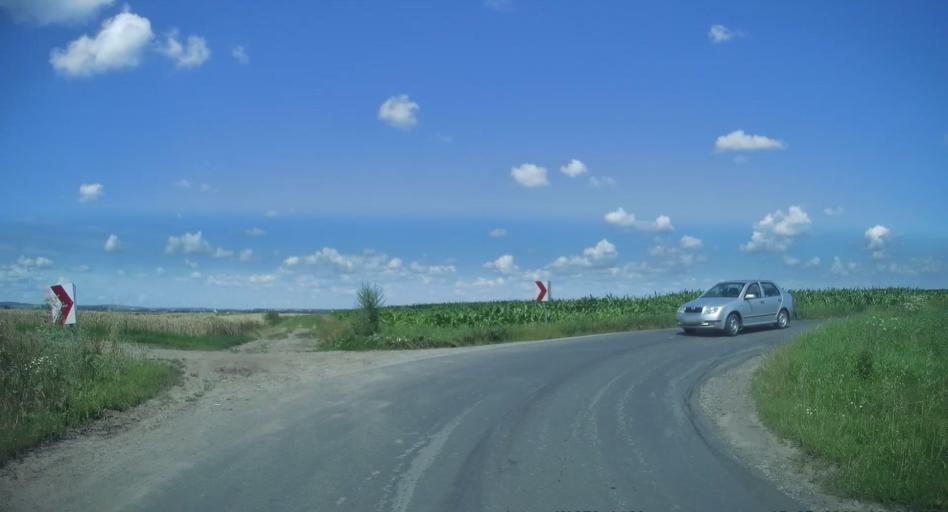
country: PL
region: Subcarpathian Voivodeship
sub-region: Powiat jaroslawski
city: Sosnica
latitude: 49.8497
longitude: 22.8772
